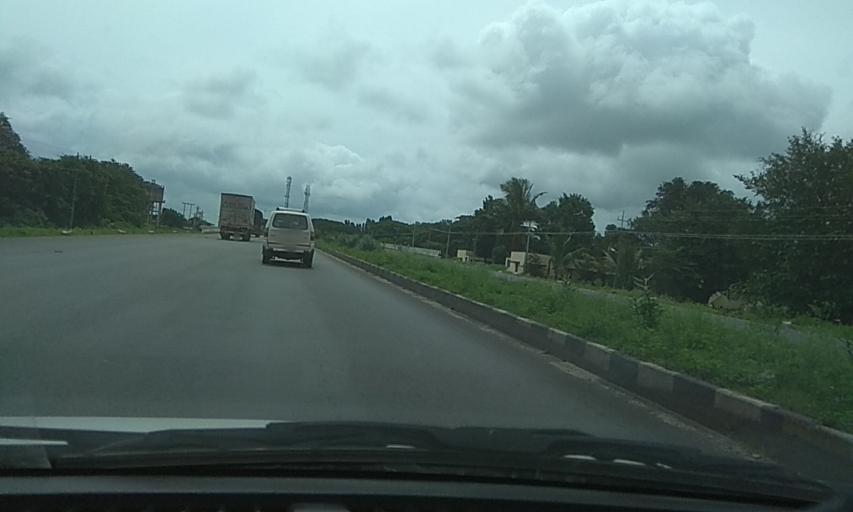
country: IN
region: Karnataka
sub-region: Davanagere
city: Mayakonda
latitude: 14.3787
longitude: 76.0946
